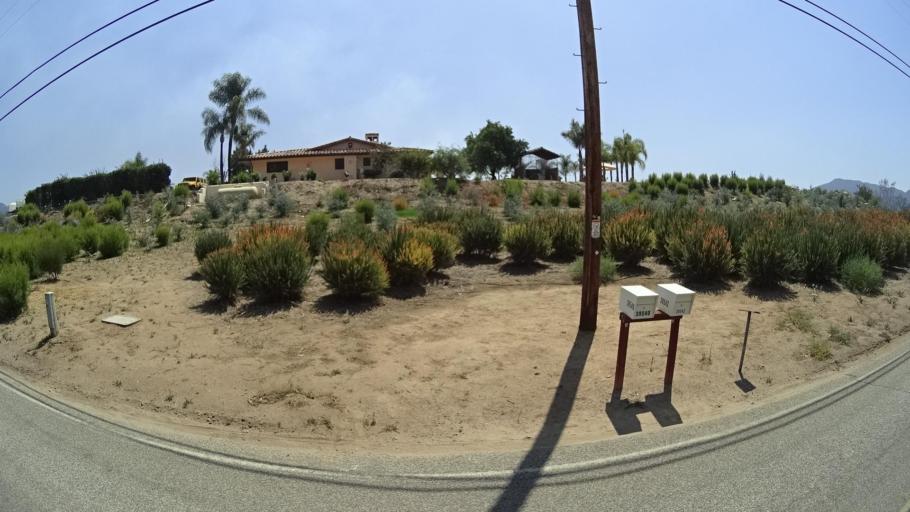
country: US
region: California
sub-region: San Diego County
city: Fallbrook
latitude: 33.4340
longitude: -117.3083
